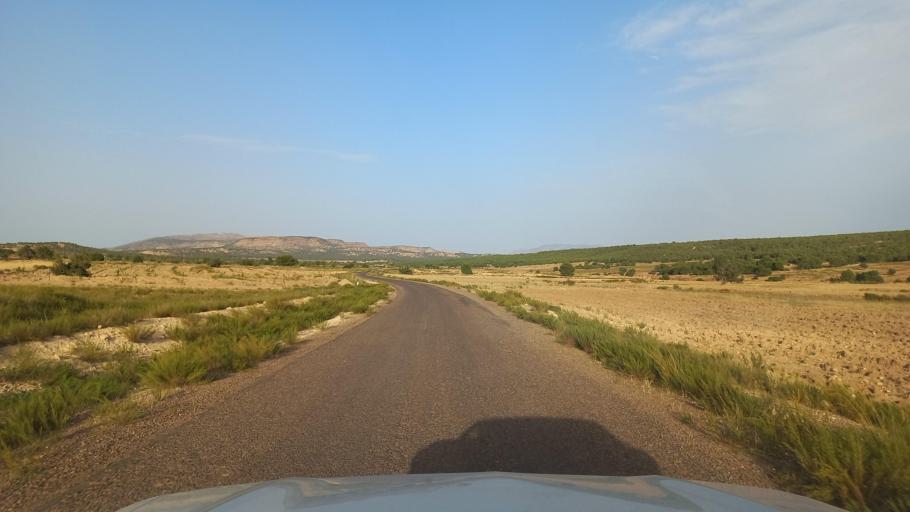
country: TN
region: Al Qasrayn
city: Sbiba
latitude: 35.4014
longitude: 8.8938
